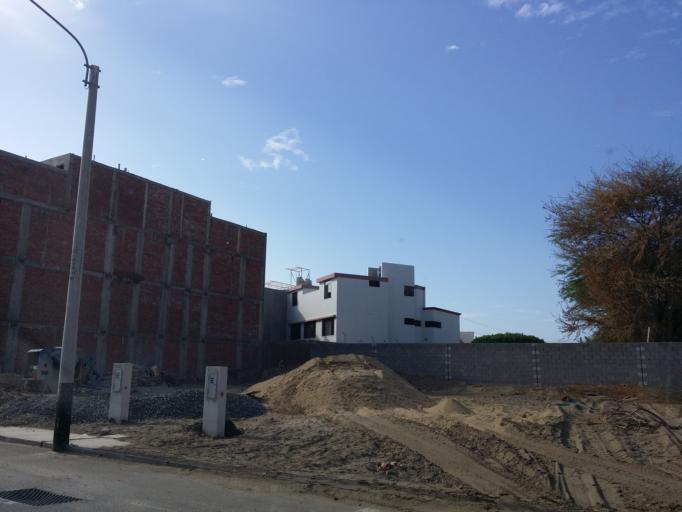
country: PE
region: Piura
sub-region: Provincia de Piura
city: Piura
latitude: -5.1751
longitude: -80.6247
